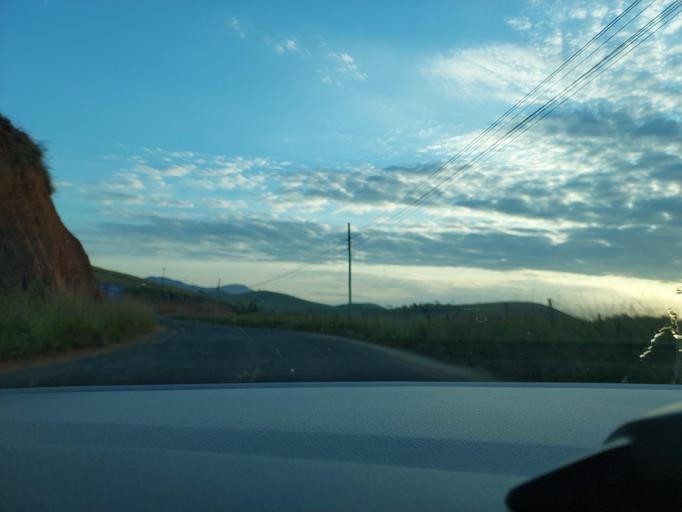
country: BR
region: Rio de Janeiro
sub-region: Natividade
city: Natividade
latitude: -21.1913
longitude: -42.1117
